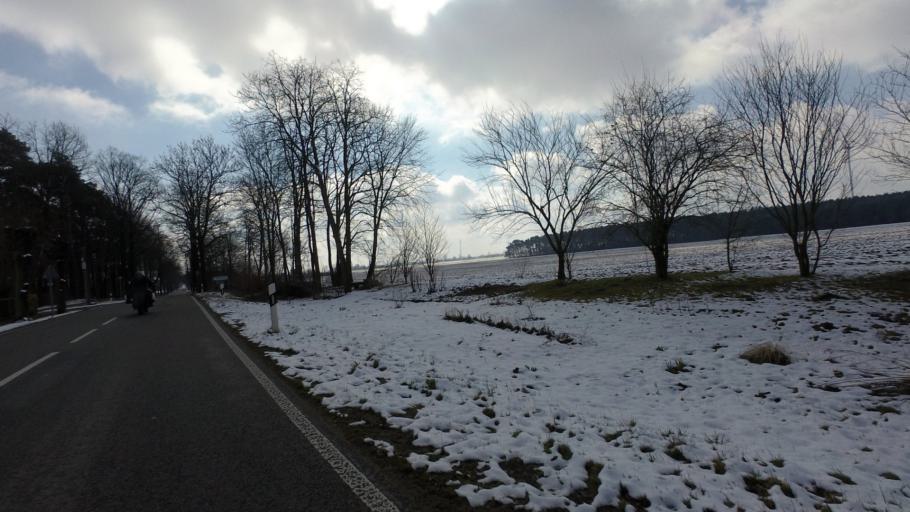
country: DE
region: Brandenburg
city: Rudnitz
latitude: 52.7021
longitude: 13.6483
